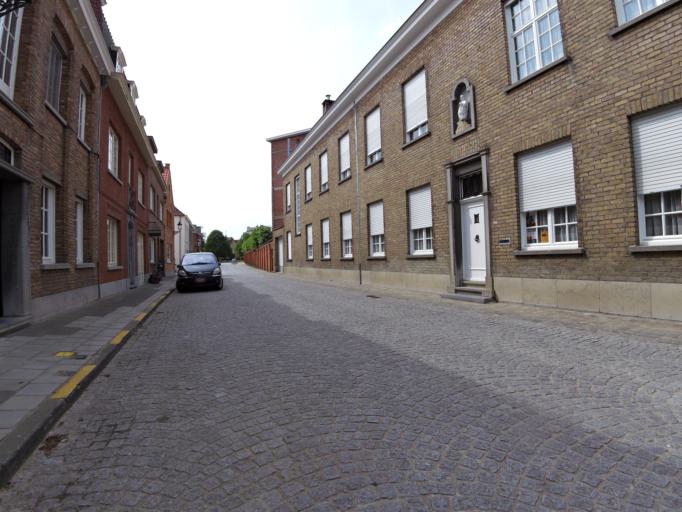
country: BE
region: Flanders
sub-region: Provincie West-Vlaanderen
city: Brugge
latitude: 51.2190
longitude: 3.2234
